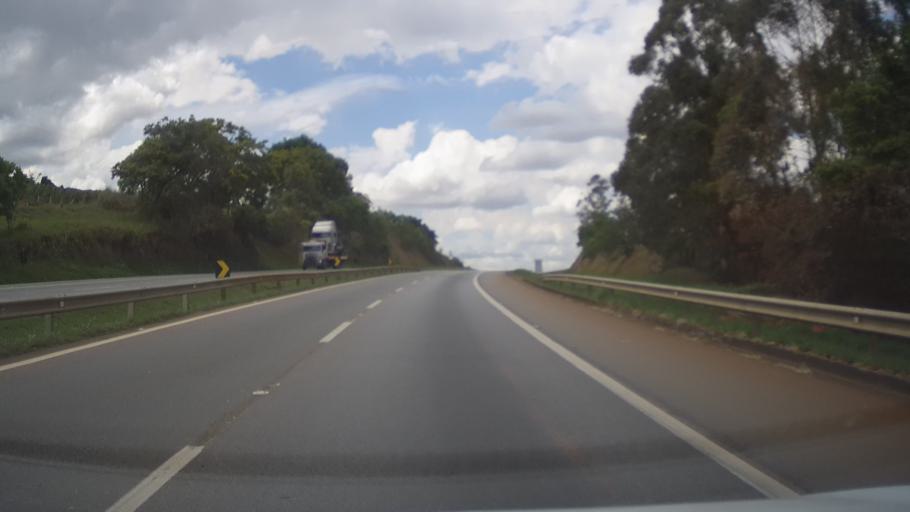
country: BR
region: Minas Gerais
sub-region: Nepomuceno
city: Nepomuceno
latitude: -21.2478
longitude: -45.1380
